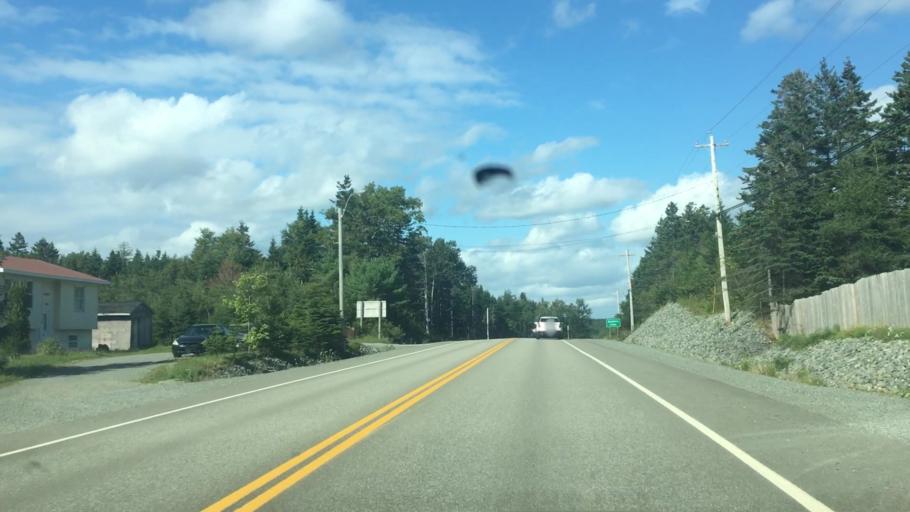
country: CA
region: Nova Scotia
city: Princeville
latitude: 45.6887
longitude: -60.7529
